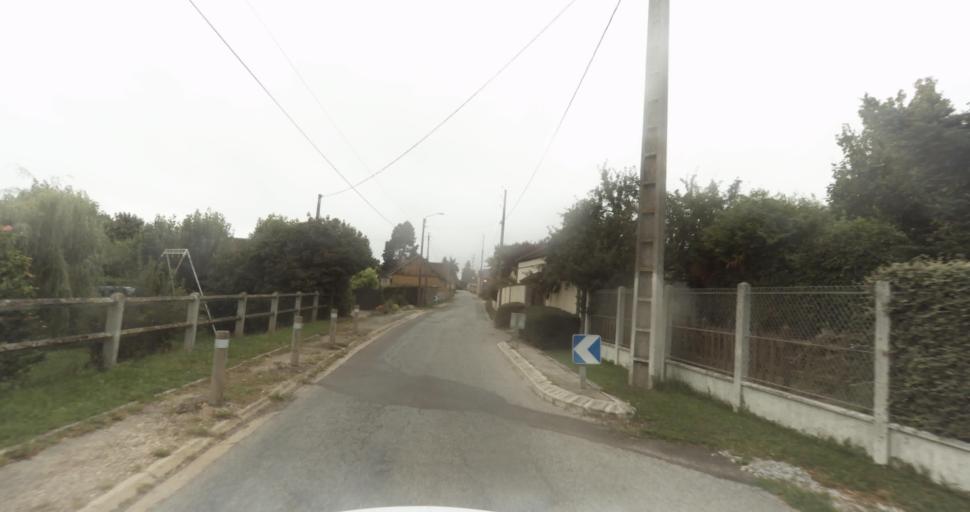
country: FR
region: Haute-Normandie
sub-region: Departement de l'Eure
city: Saint-Germain-sur-Avre
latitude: 48.7651
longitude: 1.2701
